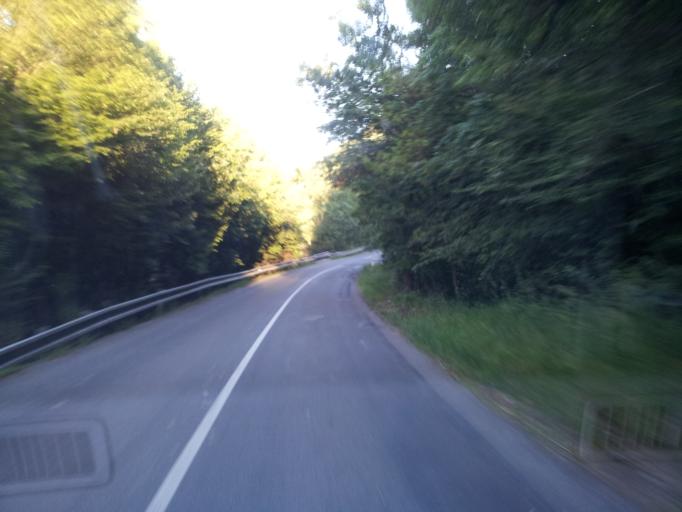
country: SK
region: Banskobystricky
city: Svaety Anton
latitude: 48.3335
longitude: 18.9584
